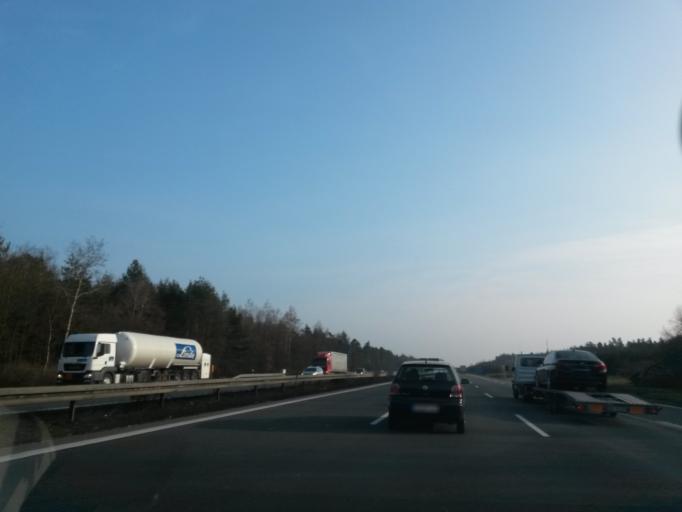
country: DE
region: Bavaria
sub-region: Regierungsbezirk Mittelfranken
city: Feucht
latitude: 49.3461
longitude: 11.2037
